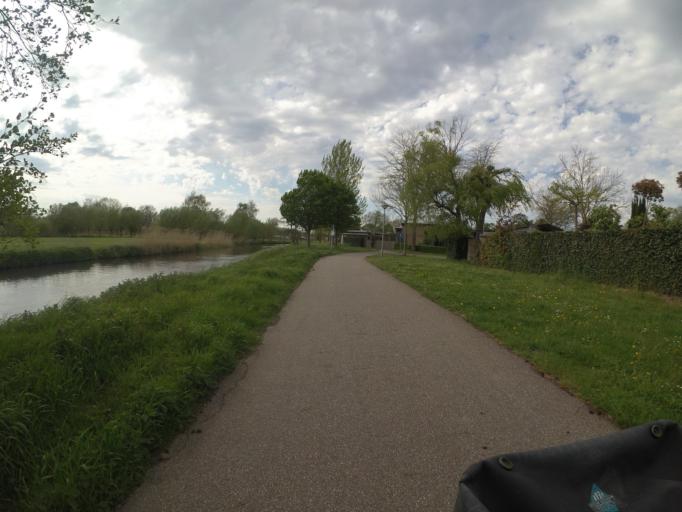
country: NL
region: North Brabant
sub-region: Gemeente Boxtel
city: Boxtel
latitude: 51.5817
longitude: 5.3401
